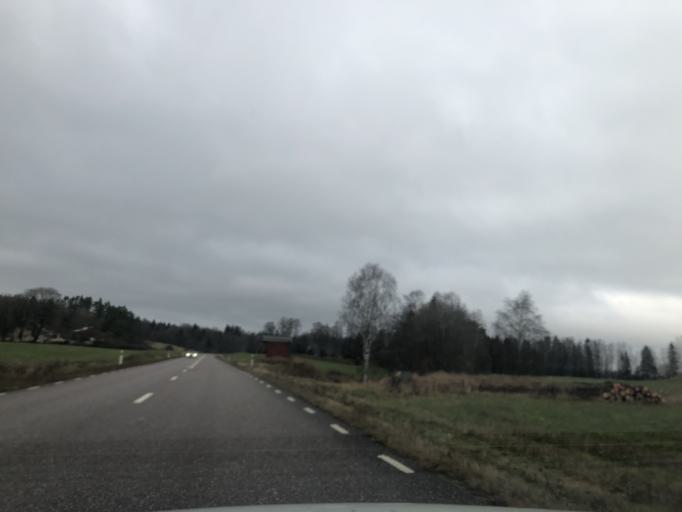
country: SE
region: Vaestra Goetaland
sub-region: Ulricehamns Kommun
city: Ulricehamn
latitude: 57.8784
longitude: 13.4344
